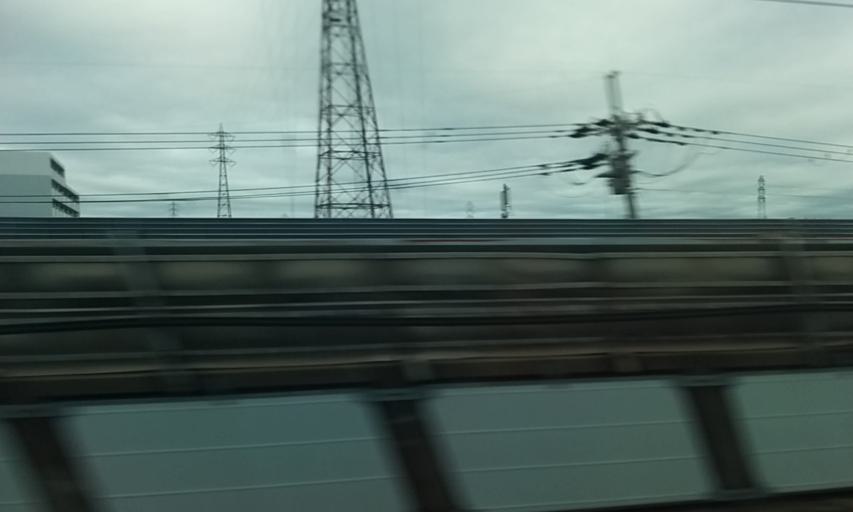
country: JP
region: Hyogo
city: Itami
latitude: 34.7680
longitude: 135.3943
